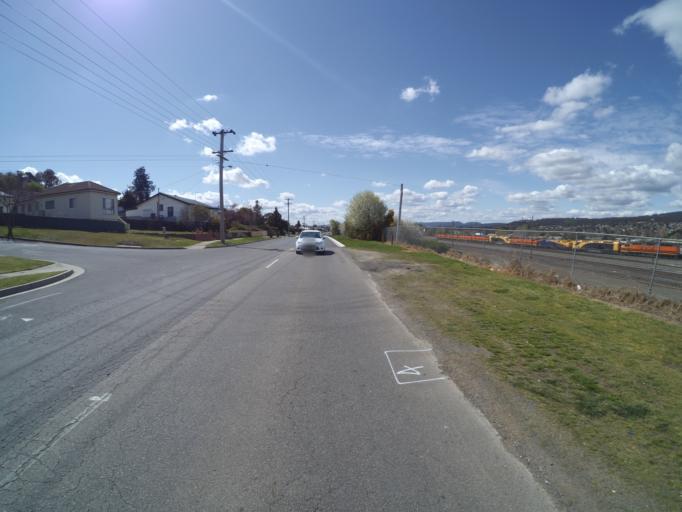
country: AU
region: New South Wales
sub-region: Goulburn Mulwaree
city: Goulburn
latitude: -34.7680
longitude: 149.7116
